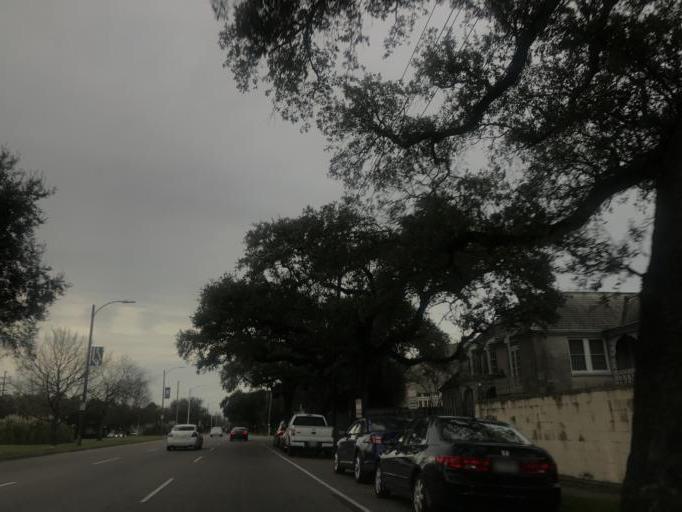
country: US
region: Louisiana
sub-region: Orleans Parish
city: New Orleans
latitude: 29.9472
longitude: -90.1141
